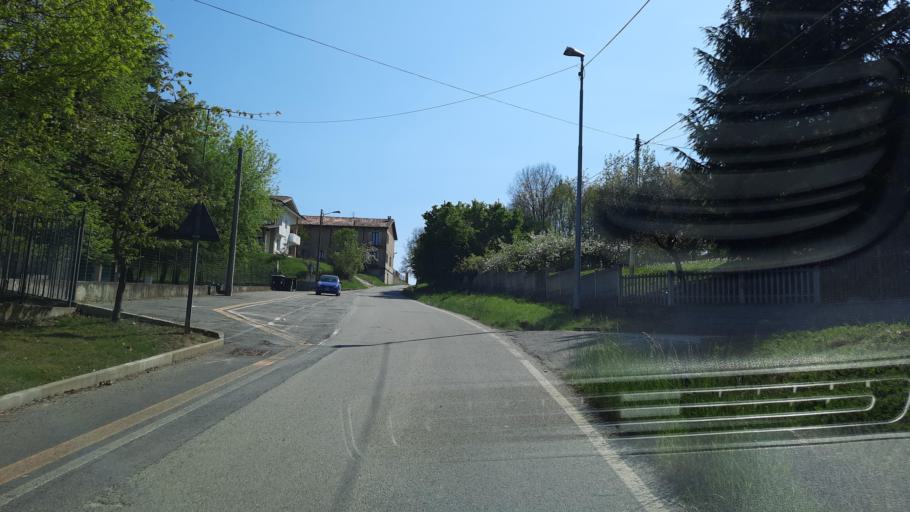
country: IT
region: Piedmont
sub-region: Provincia di Torino
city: Valentino
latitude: 45.1537
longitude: 8.0933
